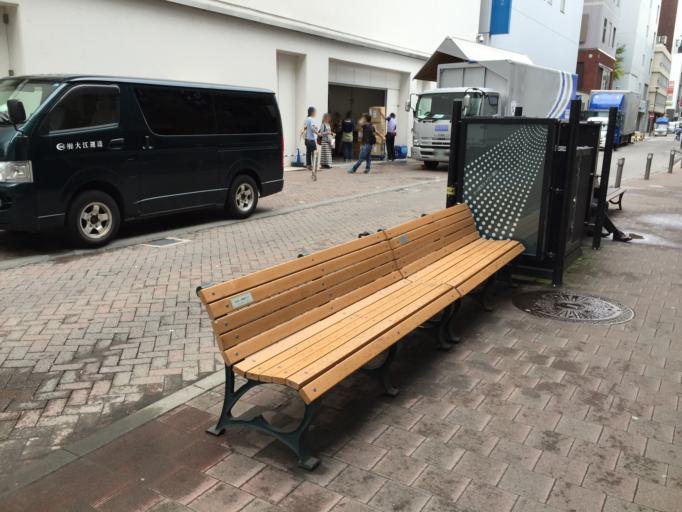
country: JP
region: Hokkaido
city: Sapporo
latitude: 43.0584
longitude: 141.3533
